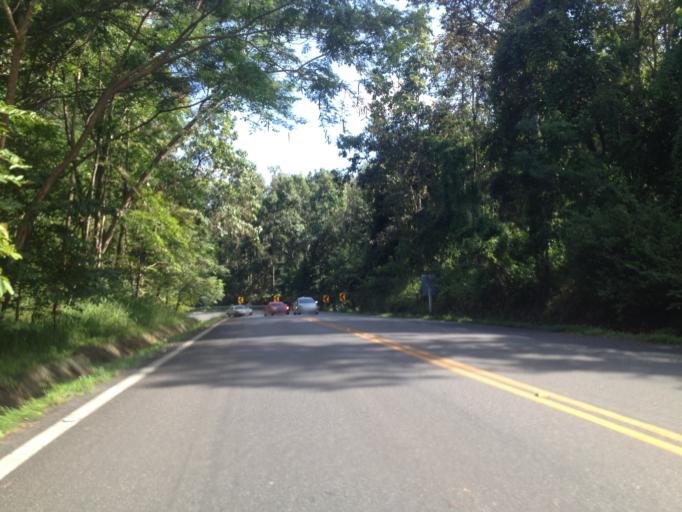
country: TH
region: Chiang Mai
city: Chiang Mai
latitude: 18.8139
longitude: 98.9376
